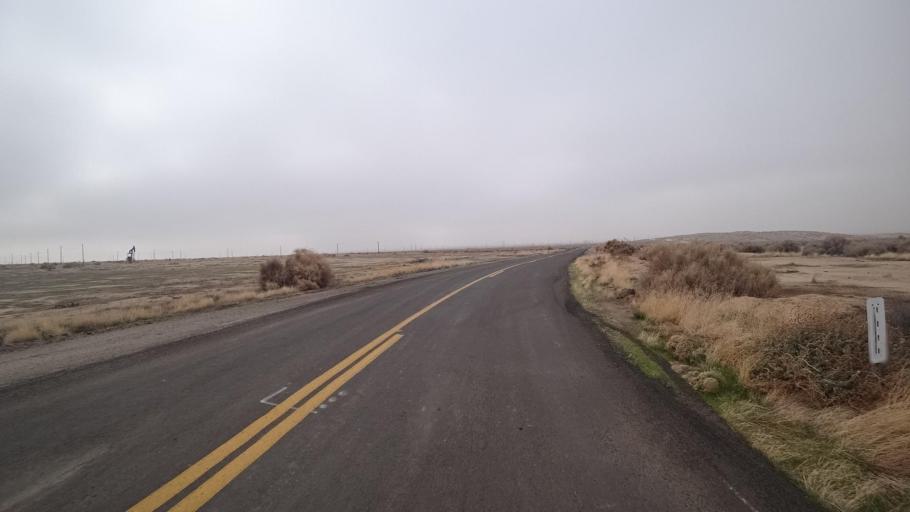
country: US
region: California
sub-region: Kern County
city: Maricopa
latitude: 35.0755
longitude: -119.3525
